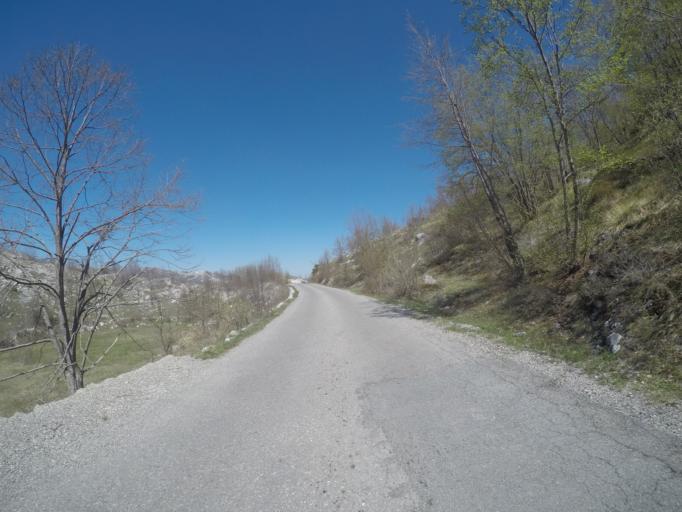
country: ME
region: Cetinje
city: Cetinje
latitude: 42.4436
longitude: 18.8741
